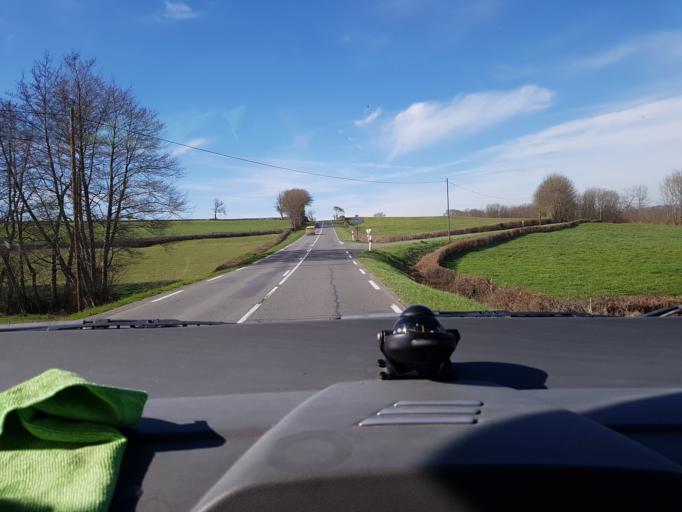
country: FR
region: Bourgogne
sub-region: Departement de Saone-et-Loire
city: Digoin
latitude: 46.5147
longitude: 4.0350
